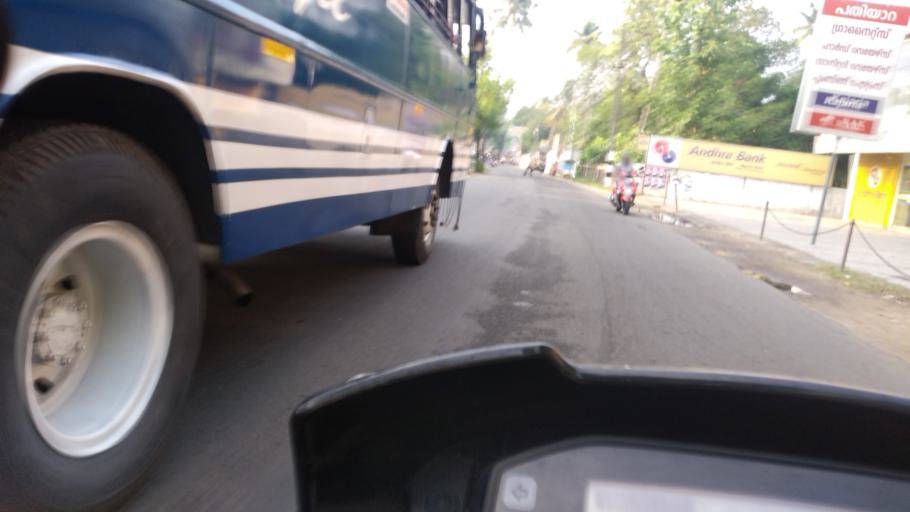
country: IN
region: Kerala
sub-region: Ernakulam
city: Elur
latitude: 10.0529
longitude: 76.2153
